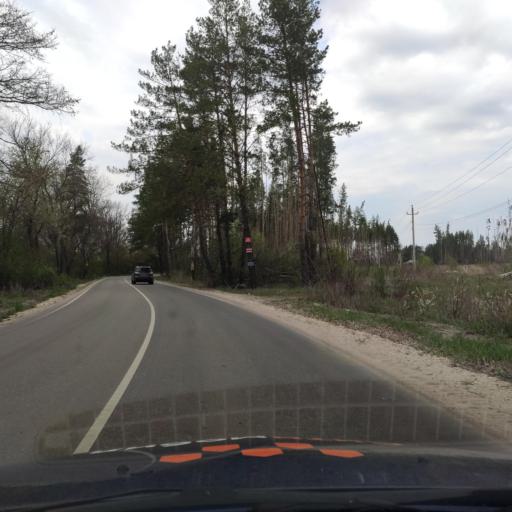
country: RU
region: Voronezj
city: Podgornoye
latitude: 51.8286
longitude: 39.1442
